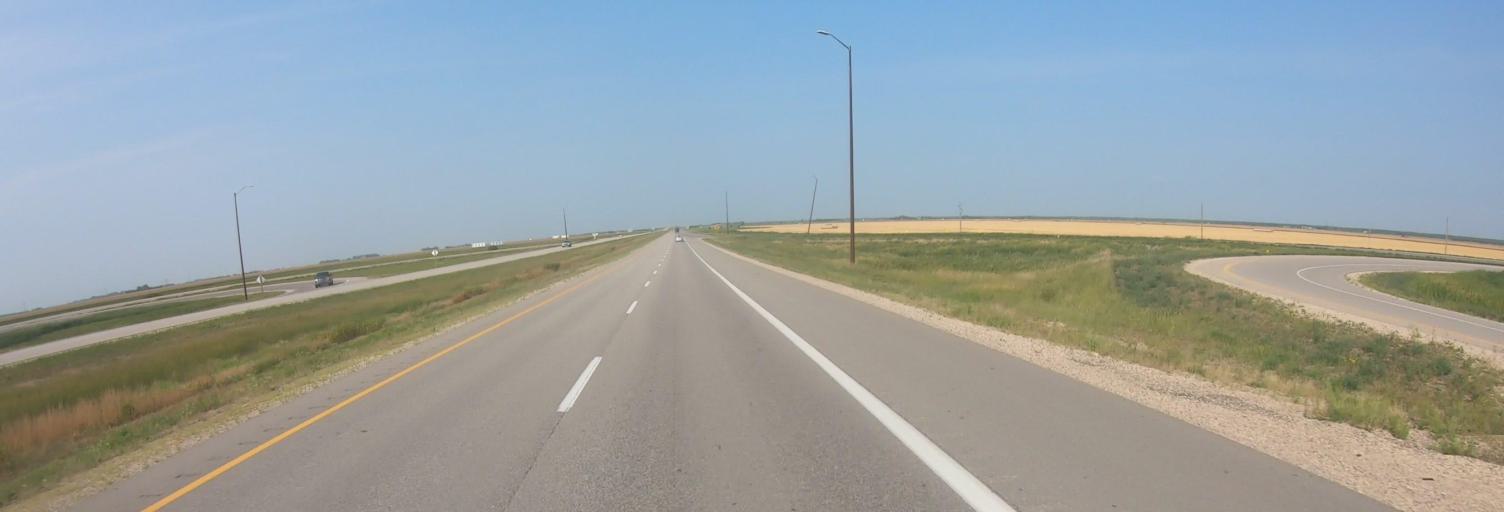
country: CA
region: Manitoba
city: Steinbach
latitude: 49.6805
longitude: -96.6596
